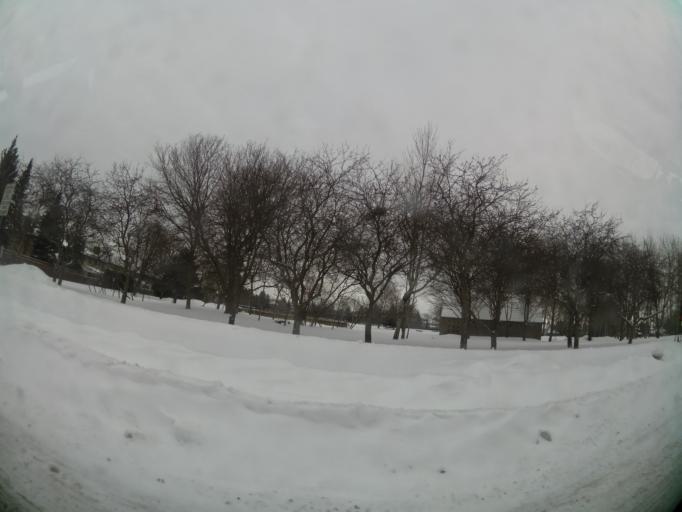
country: CA
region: Ontario
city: Ottawa
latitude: 45.3699
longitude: -75.6204
